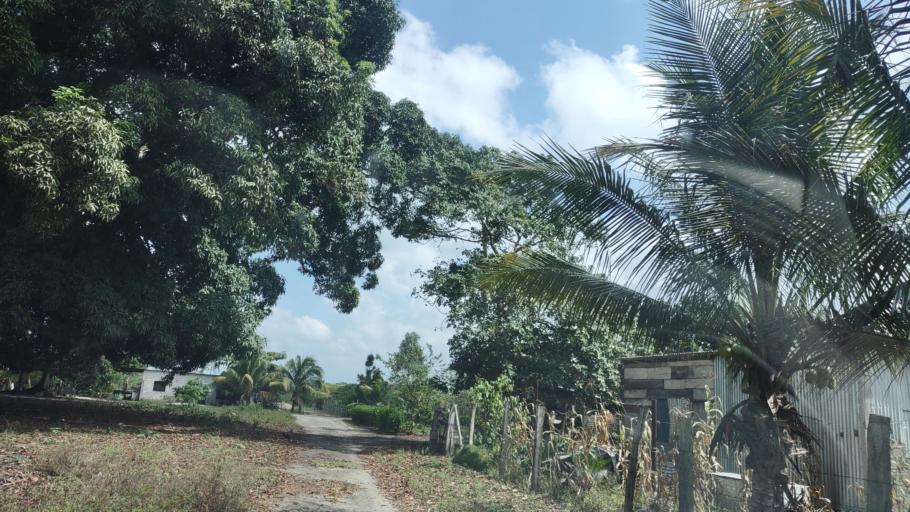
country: MX
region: Veracruz
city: Las Choapas
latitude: 17.9477
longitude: -94.0943
